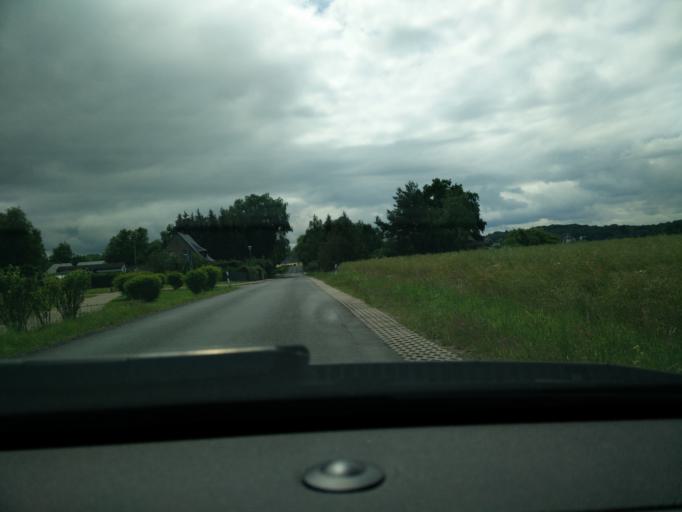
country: DE
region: Saxony
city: Bad Lausick
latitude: 51.1567
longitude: 12.6640
